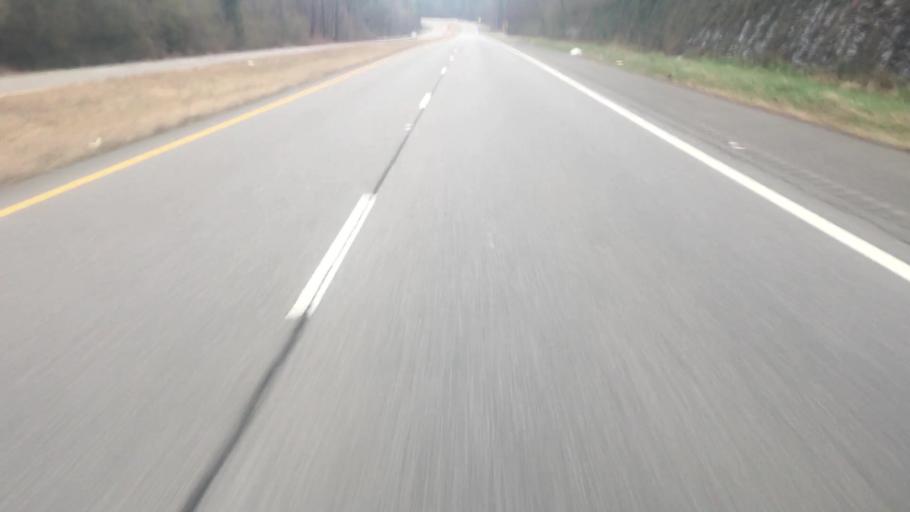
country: US
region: Alabama
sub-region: Walker County
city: Cordova
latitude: 33.8240
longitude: -87.1933
